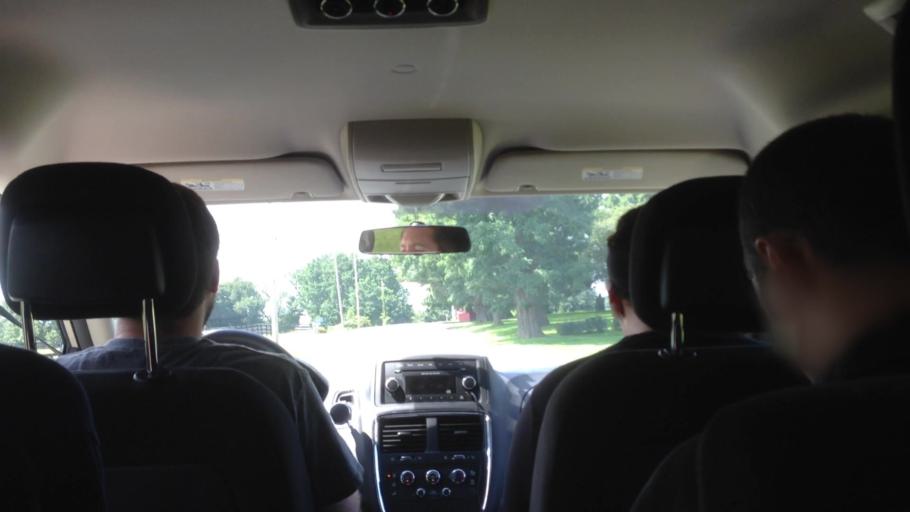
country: US
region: New York
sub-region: Dutchess County
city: Tivoli
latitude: 42.0448
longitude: -73.8617
